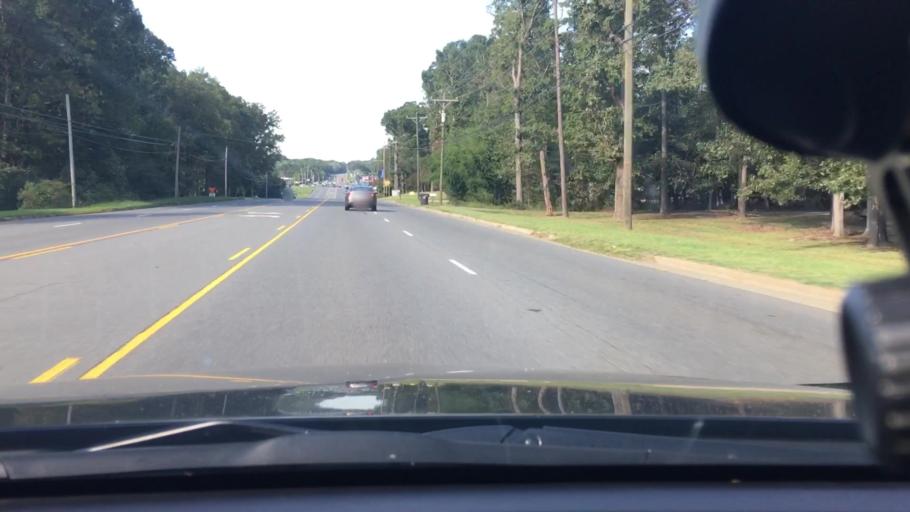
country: US
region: North Carolina
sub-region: Cabarrus County
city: Midland
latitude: 35.2529
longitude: -80.4940
